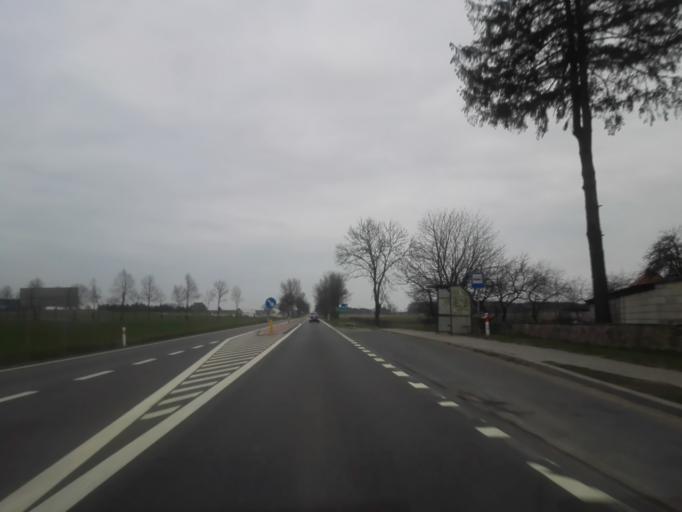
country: PL
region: Podlasie
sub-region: Powiat kolnenski
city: Stawiski
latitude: 53.4615
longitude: 22.1968
